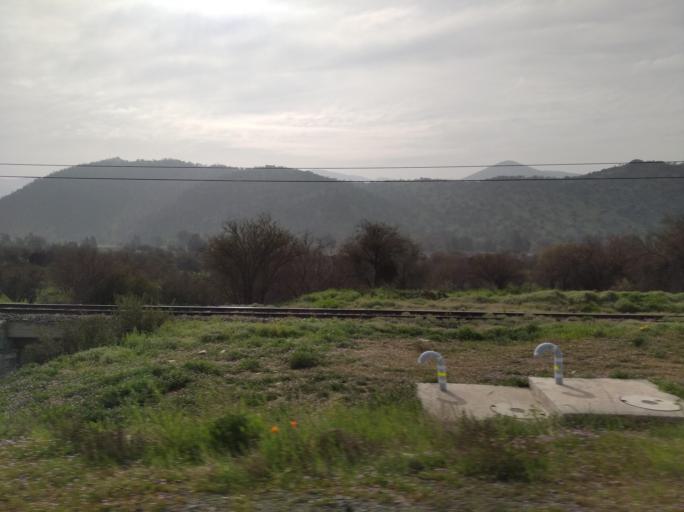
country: CL
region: Santiago Metropolitan
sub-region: Provincia de Chacabuco
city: Lampa
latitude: -33.1424
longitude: -70.9155
